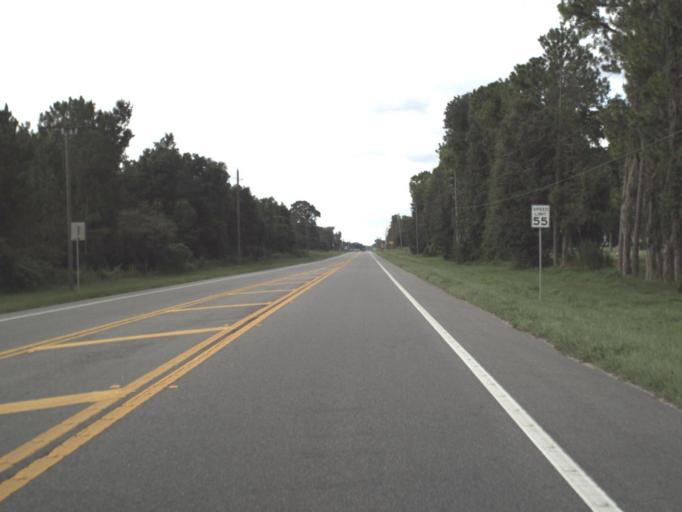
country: US
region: Florida
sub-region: Hernando County
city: Ridge Manor
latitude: 28.5168
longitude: -82.1682
